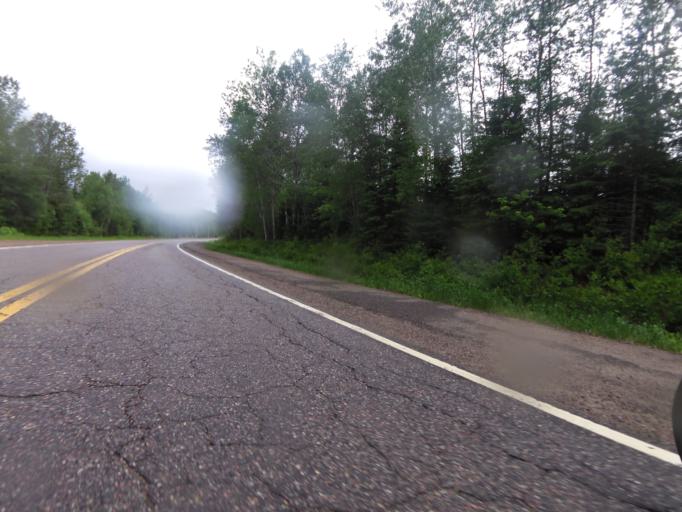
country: CA
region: Quebec
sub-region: Outaouais
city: Shawville
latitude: 45.9123
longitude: -76.2577
